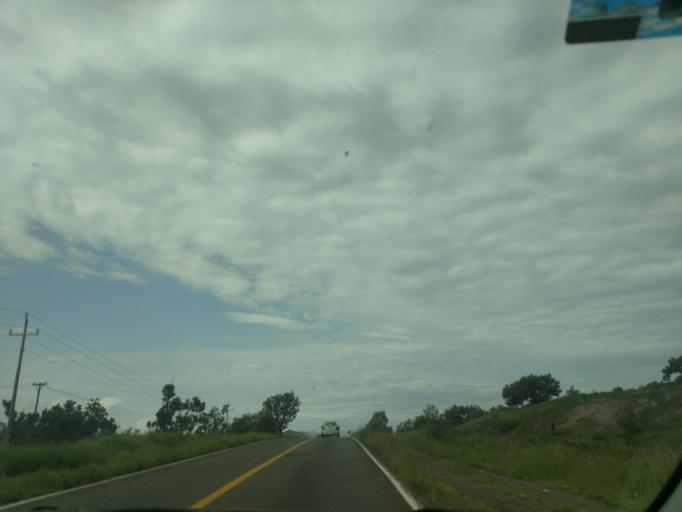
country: MX
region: Jalisco
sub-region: Atengo
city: Soyatlan del Oro
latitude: 20.5494
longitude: -104.3029
